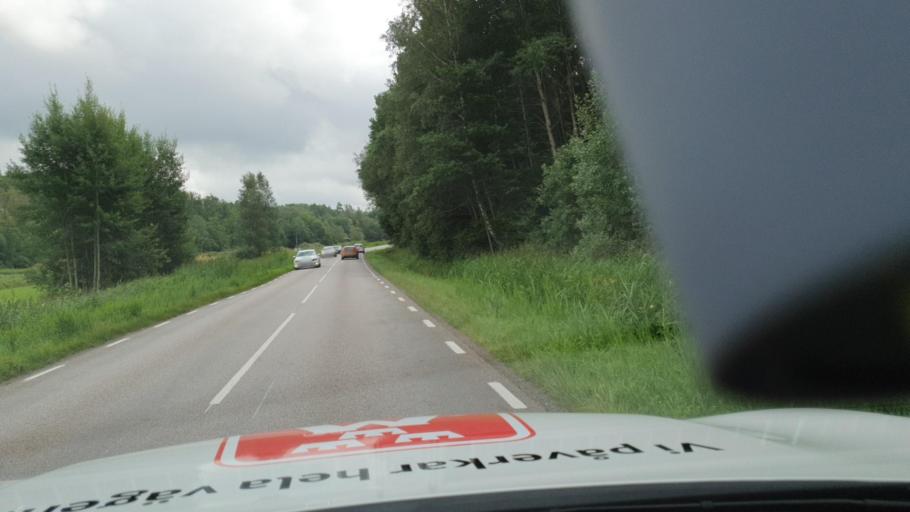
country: SE
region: Vaestra Goetaland
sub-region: Tanums Kommun
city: Grebbestad
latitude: 58.6605
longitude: 11.3039
